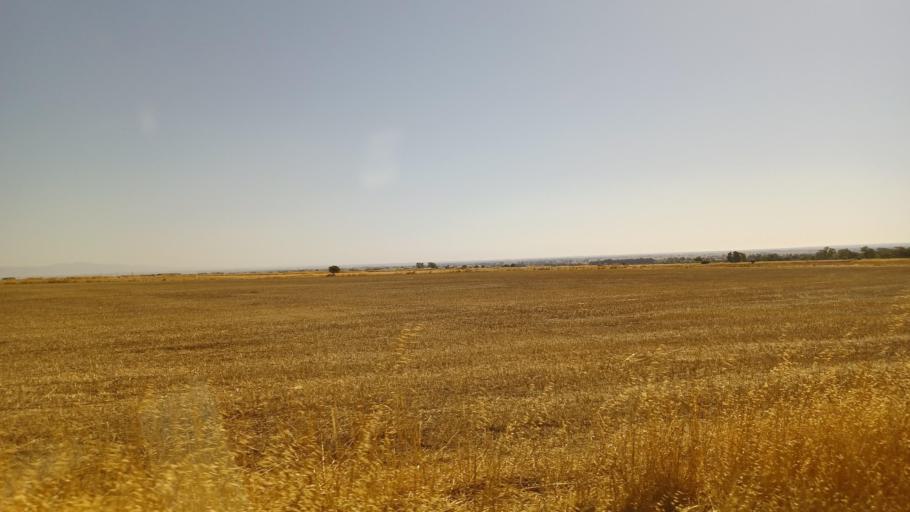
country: CY
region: Larnaka
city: Pergamos
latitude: 35.0427
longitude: 33.6823
